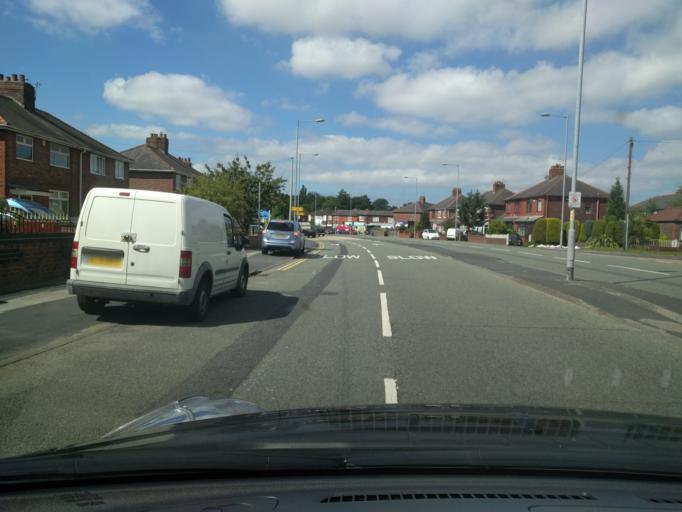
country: GB
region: England
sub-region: Warrington
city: Grappenhall
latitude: 53.3986
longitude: -2.5430
